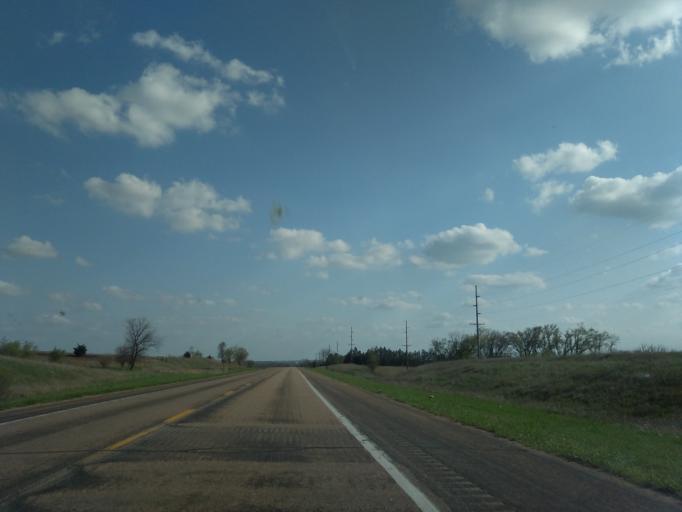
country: US
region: Nebraska
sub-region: Webster County
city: Red Cloud
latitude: 40.1126
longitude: -98.5189
